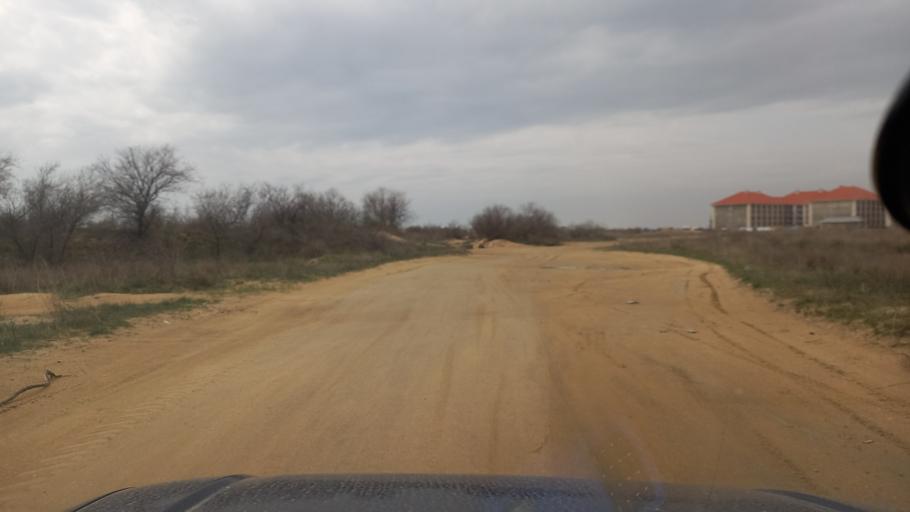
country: RU
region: Krasnodarskiy
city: Vityazevo
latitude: 44.9925
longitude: 37.2373
